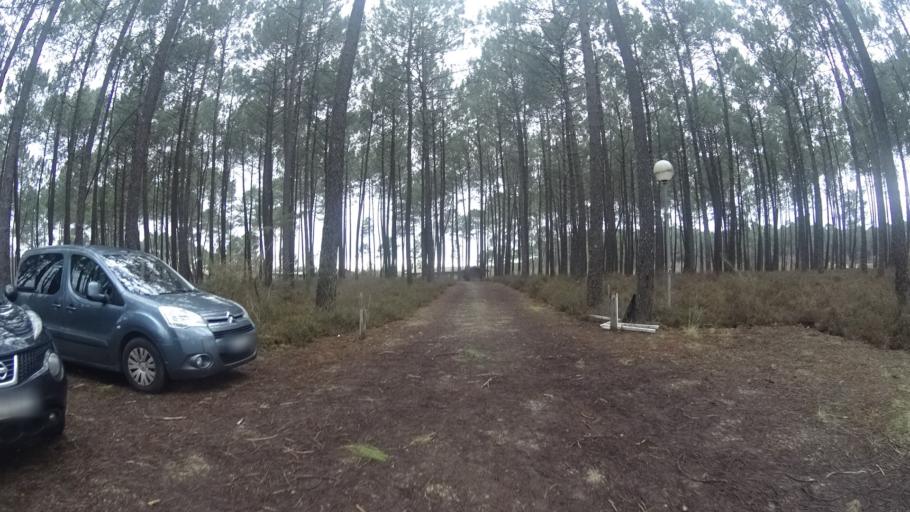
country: FR
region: Aquitaine
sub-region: Departement de la Gironde
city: Belin-Beliet
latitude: 44.5063
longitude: -0.8039
